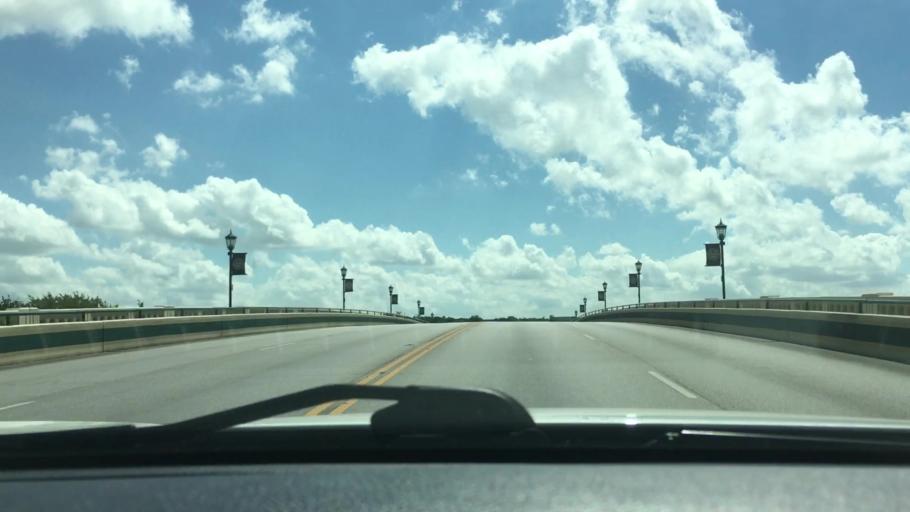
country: US
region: Texas
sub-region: Williamson County
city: Round Rock
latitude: 30.5073
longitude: -97.6784
